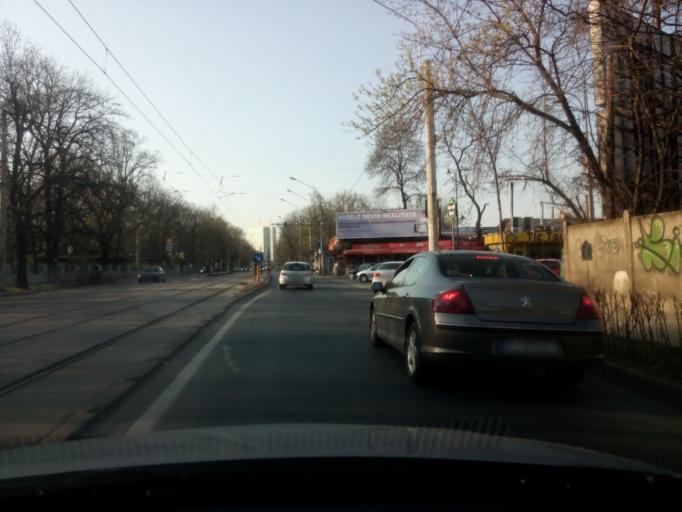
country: RO
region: Bucuresti
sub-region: Municipiul Bucuresti
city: Bucuresti
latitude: 44.4710
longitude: 26.0728
